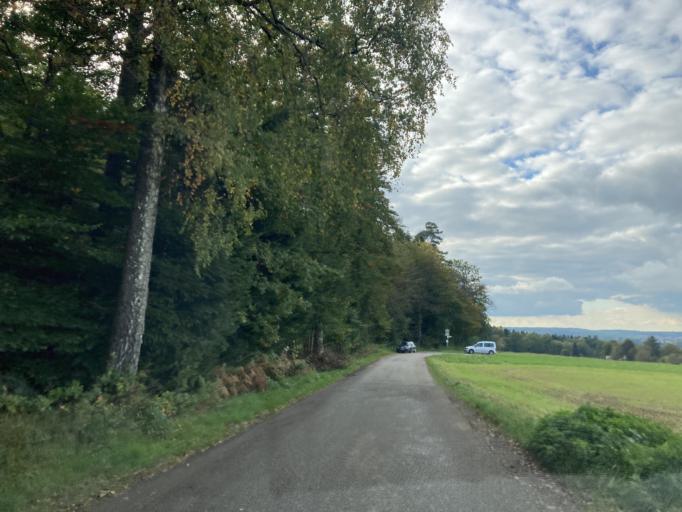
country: DE
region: Baden-Wuerttemberg
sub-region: Karlsruhe Region
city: Dobel
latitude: 48.8356
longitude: 8.5317
